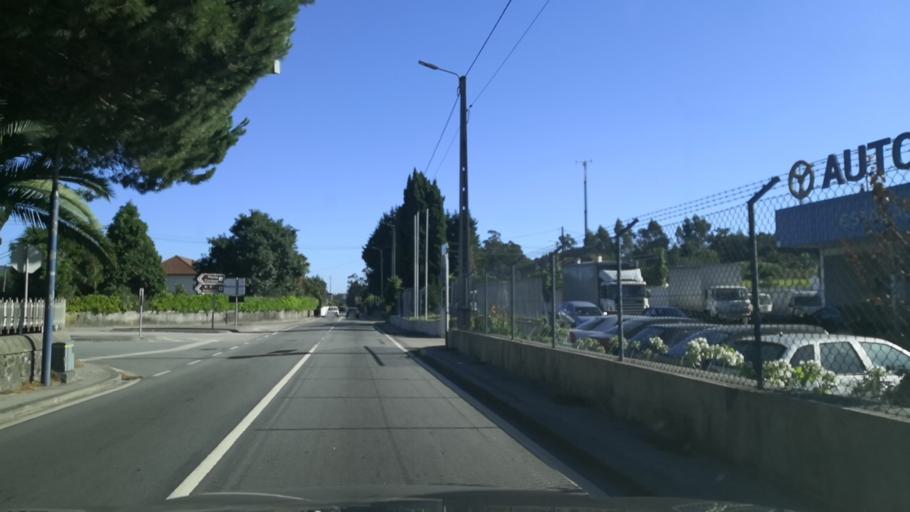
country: PT
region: Porto
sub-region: Santo Tirso
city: Sao Miguel do Couto
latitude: 41.2974
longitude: -8.4710
